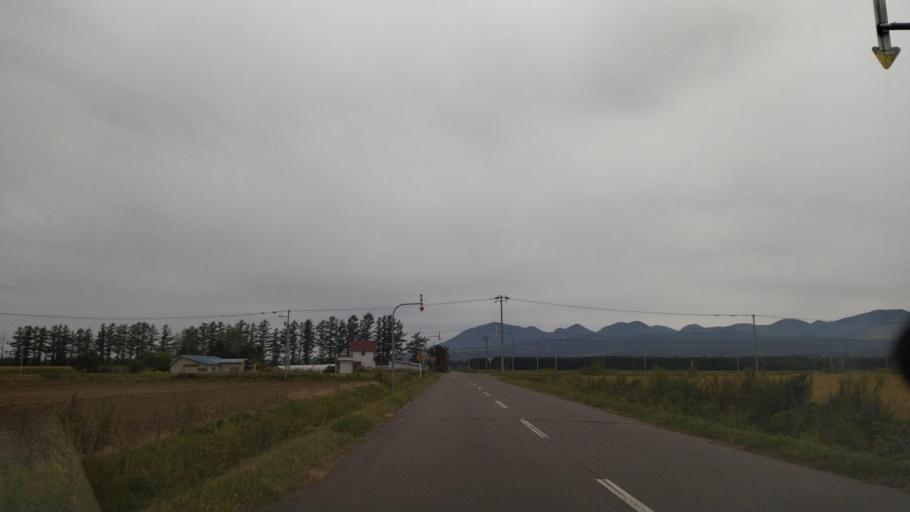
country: JP
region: Hokkaido
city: Otofuke
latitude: 43.2165
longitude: 143.2790
